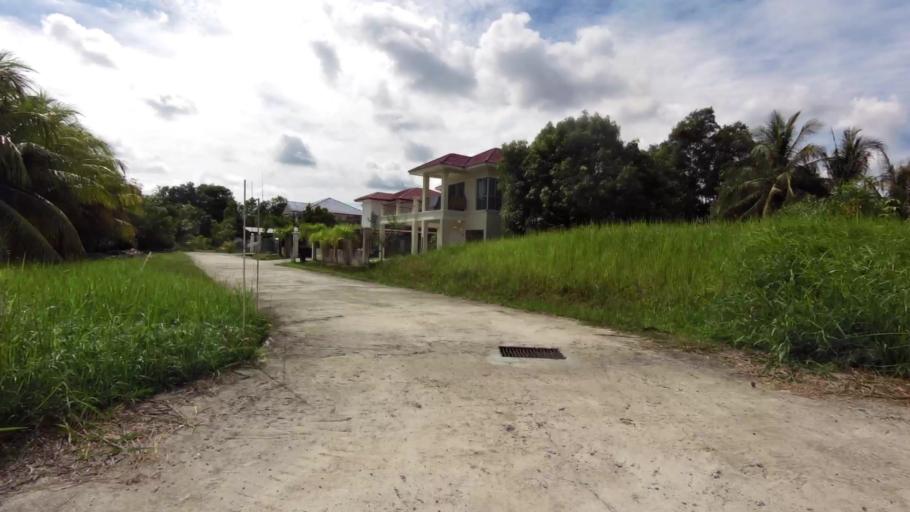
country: BN
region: Brunei and Muara
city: Bandar Seri Begawan
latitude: 4.9361
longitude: 114.9099
